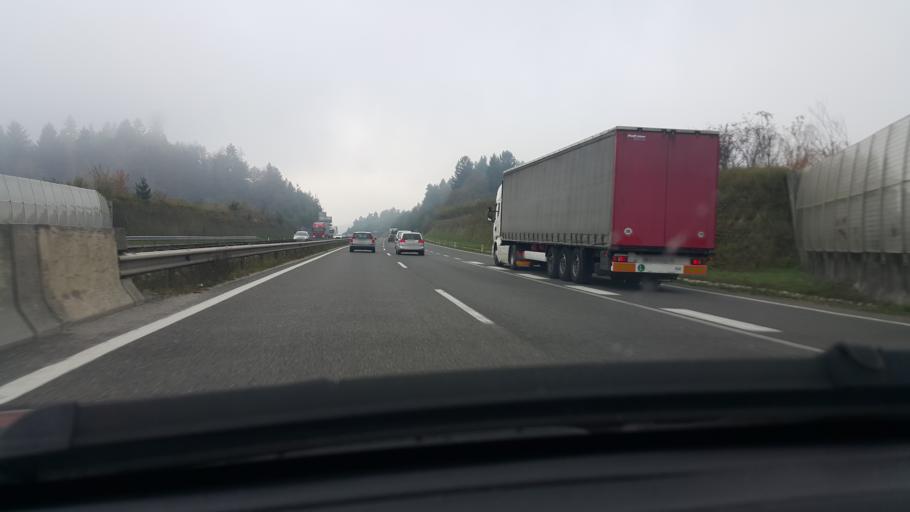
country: SI
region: Skofljica
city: Lavrica
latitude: 46.0385
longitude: 14.5750
